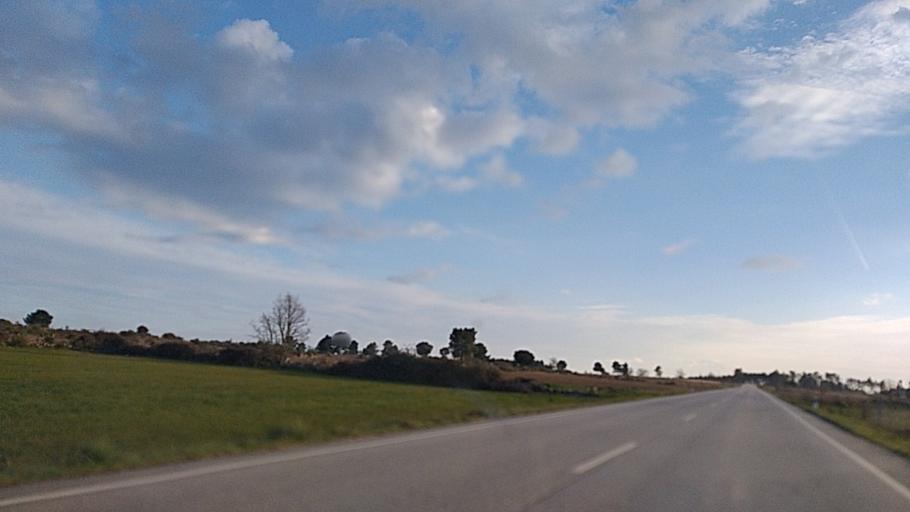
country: PT
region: Guarda
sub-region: Pinhel
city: Pinhel
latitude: 40.6504
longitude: -6.9674
